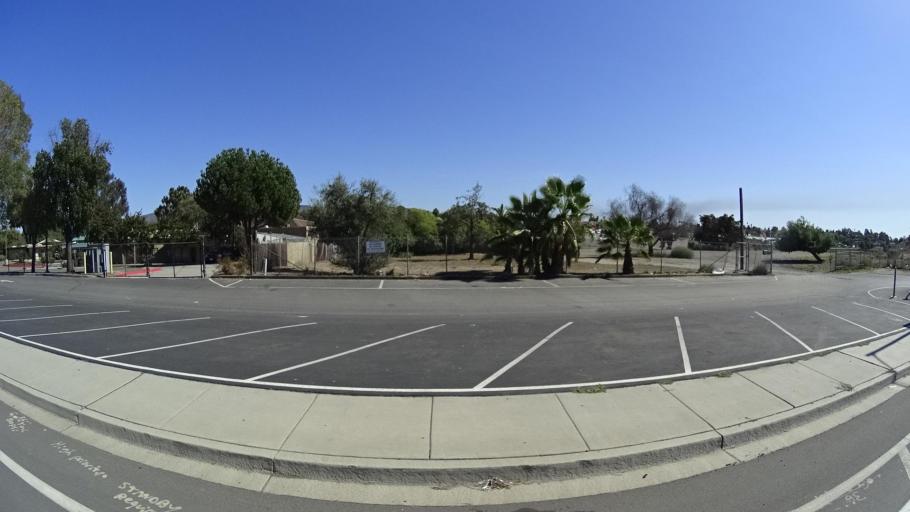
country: US
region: California
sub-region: San Diego County
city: La Presa
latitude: 32.7067
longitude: -117.0086
